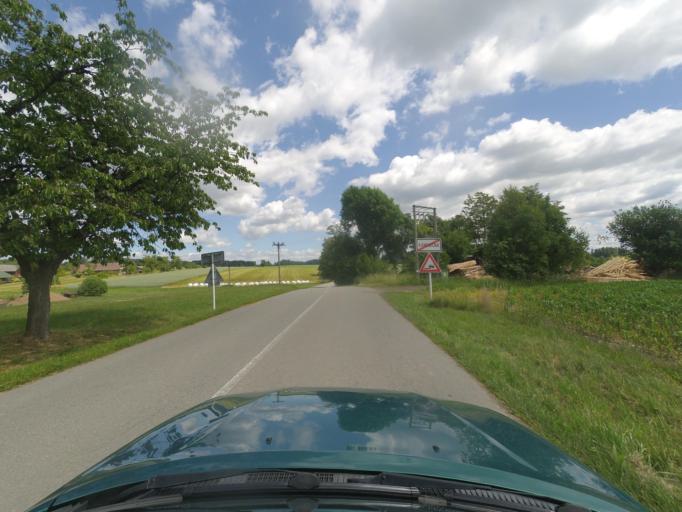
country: CZ
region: Pardubicky
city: Zamberk
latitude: 50.1201
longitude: 16.4380
